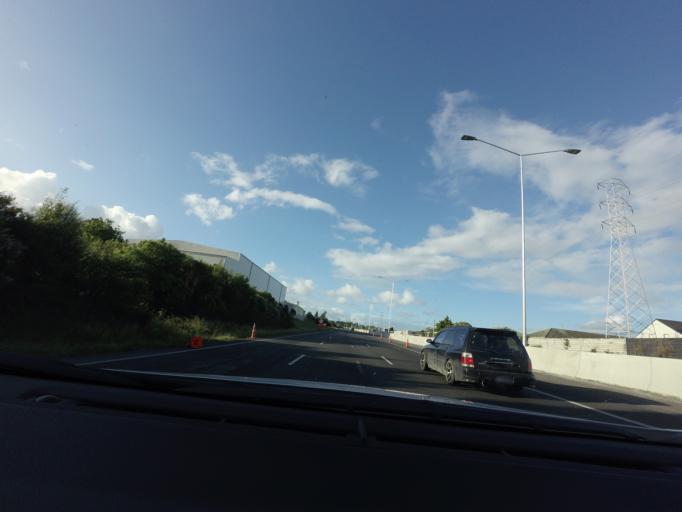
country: NZ
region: Auckland
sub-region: Auckland
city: Takanini
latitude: -37.0297
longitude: 174.9099
